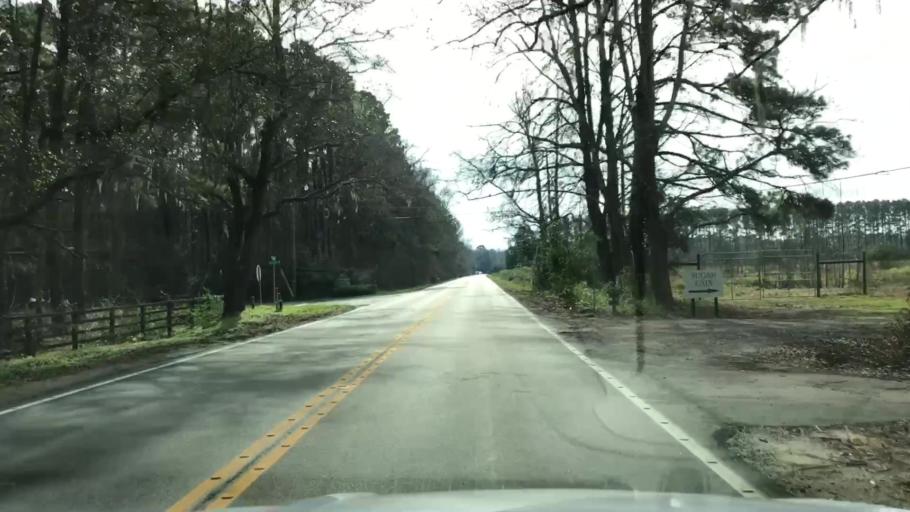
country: US
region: South Carolina
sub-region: Charleston County
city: Shell Point
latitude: 32.7248
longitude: -80.0235
